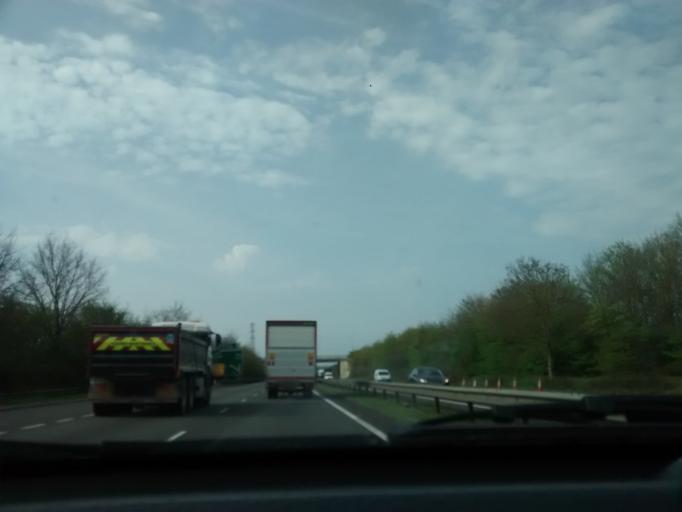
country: GB
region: England
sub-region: Oxfordshire
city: Kidlington
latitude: 51.8057
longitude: -1.2737
